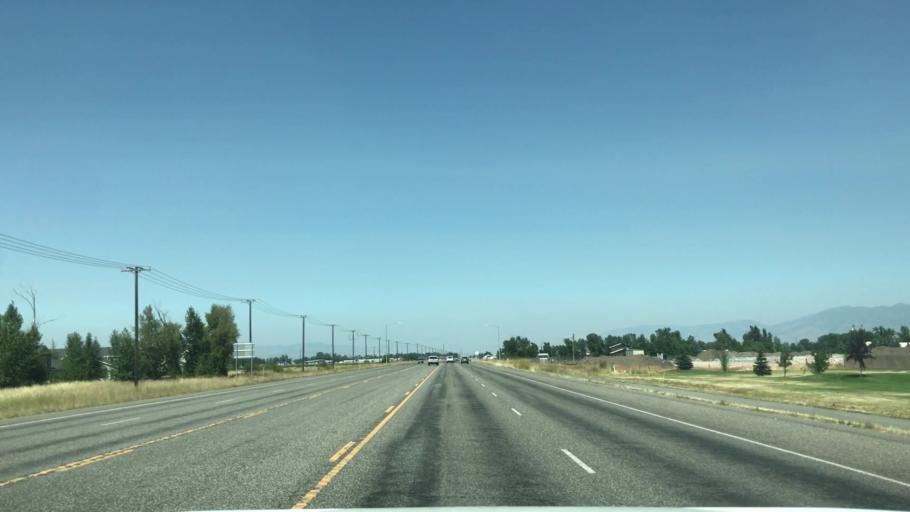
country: US
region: Montana
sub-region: Gallatin County
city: Four Corners
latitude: 45.6830
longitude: -111.1858
